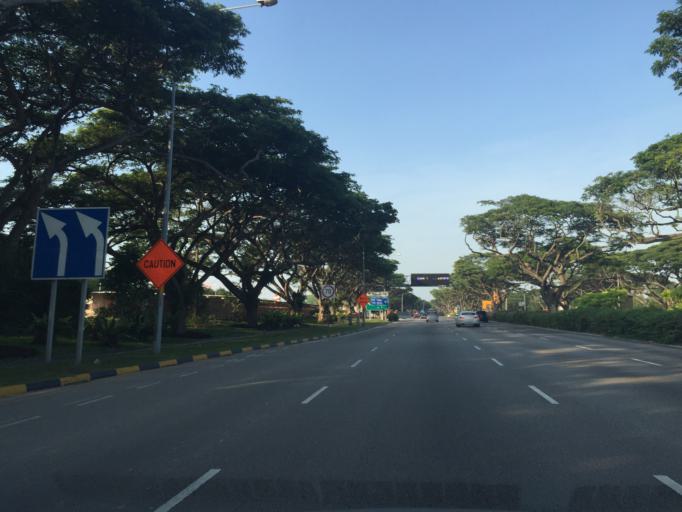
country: SG
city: Singapore
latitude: 1.3435
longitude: 103.9828
